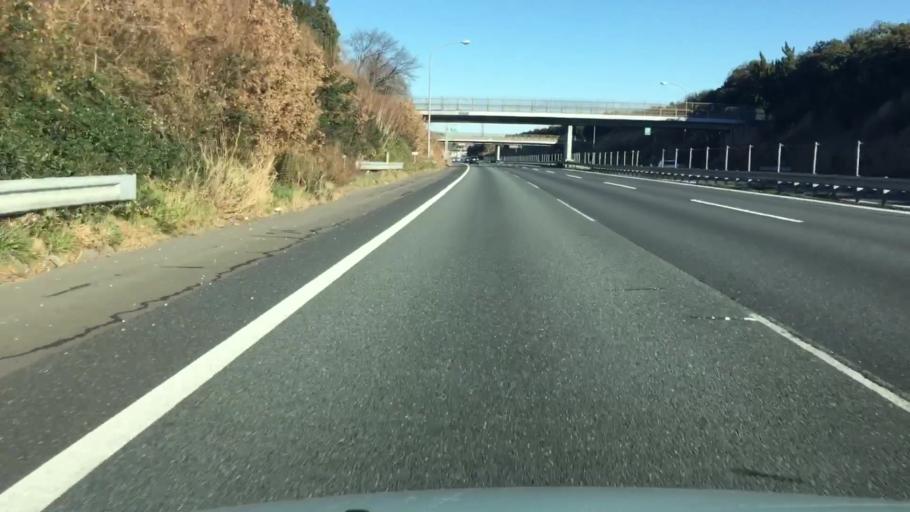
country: JP
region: Saitama
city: Sakado
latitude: 35.9929
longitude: 139.3858
